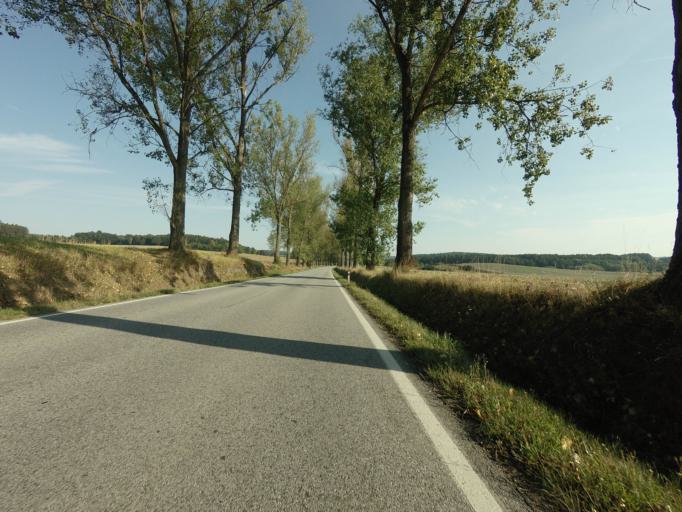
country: CZ
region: Jihocesky
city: Tyn nad Vltavou
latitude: 49.2347
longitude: 14.4208
